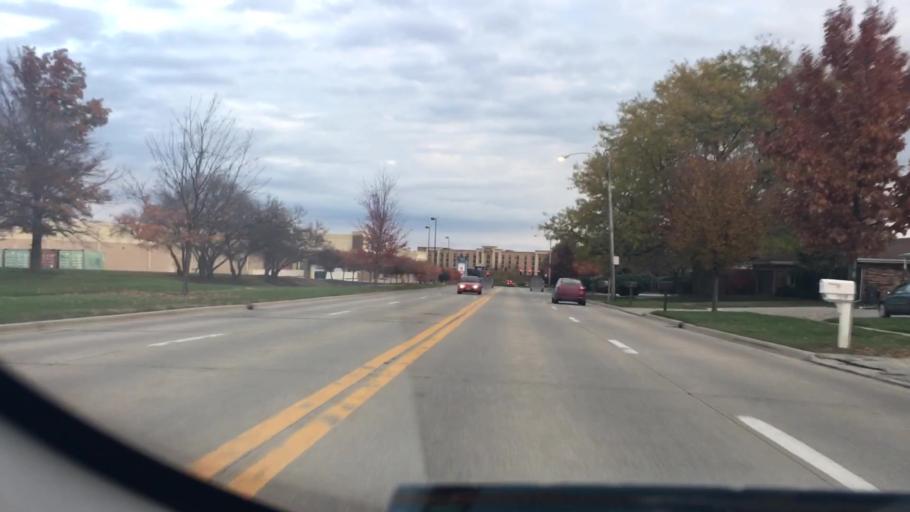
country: US
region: Illinois
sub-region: McLean County
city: Normal
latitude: 40.5073
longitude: -88.9598
